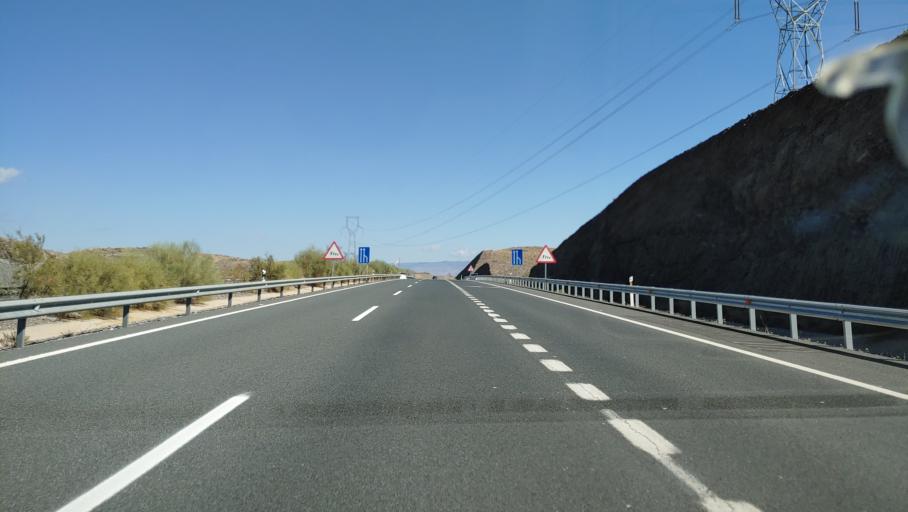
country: ES
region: Andalusia
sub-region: Provincia de Almeria
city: Gergal
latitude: 37.1246
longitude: -2.6312
